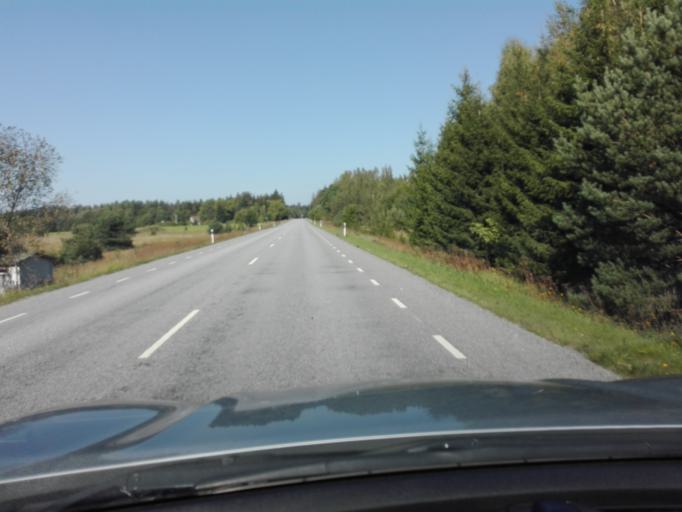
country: EE
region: Raplamaa
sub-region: Rapla vald
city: Rapla
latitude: 58.9996
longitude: 24.7689
